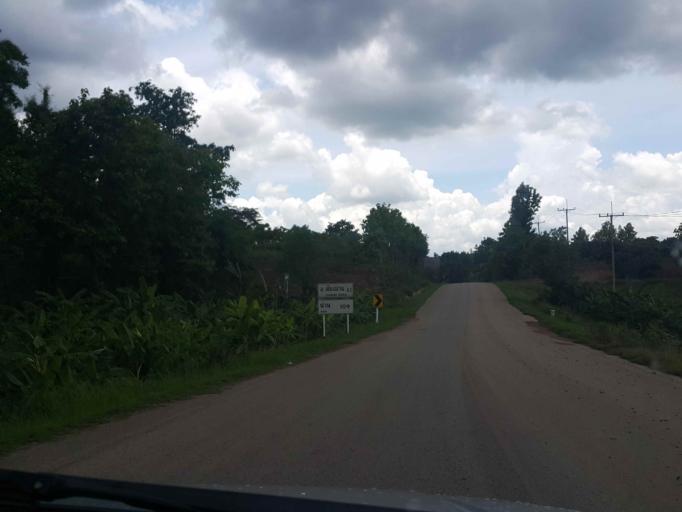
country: TH
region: Phayao
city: Dok Kham Tai
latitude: 18.9718
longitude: 100.0742
